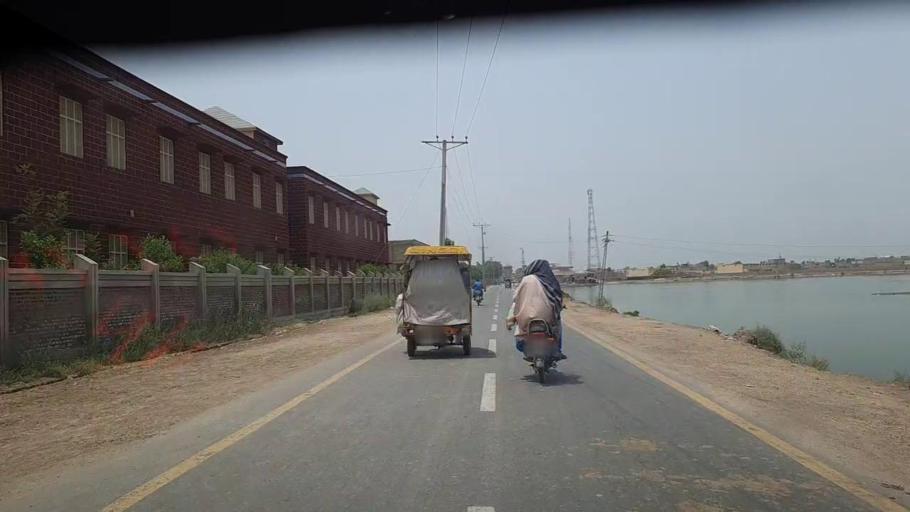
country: PK
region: Sindh
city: Sita Road
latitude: 27.0414
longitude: 67.8551
